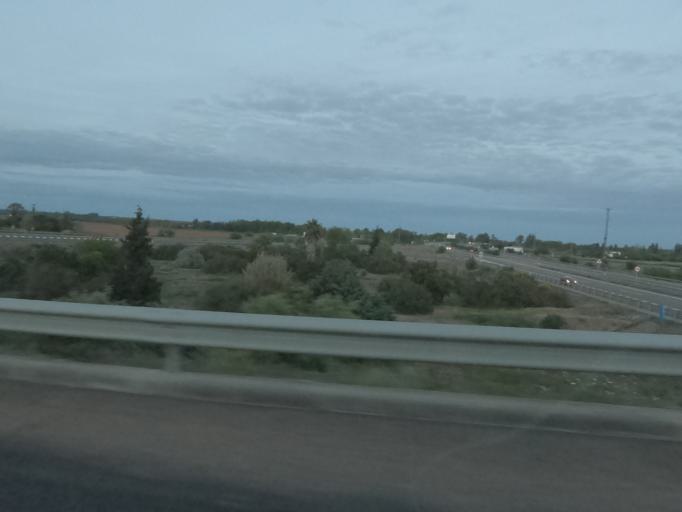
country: ES
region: Extremadura
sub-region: Provincia de Badajoz
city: Badajoz
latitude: 38.9208
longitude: -6.9647
